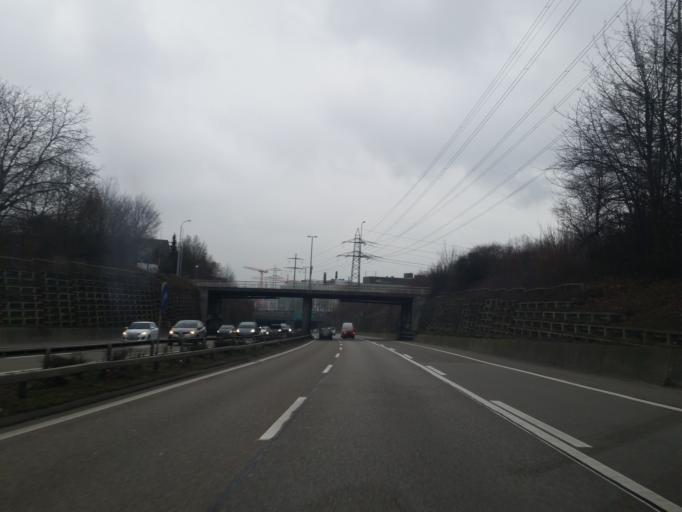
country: CH
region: Zurich
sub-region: Bezirk Buelach
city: Glattbrugg
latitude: 47.4281
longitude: 8.5548
